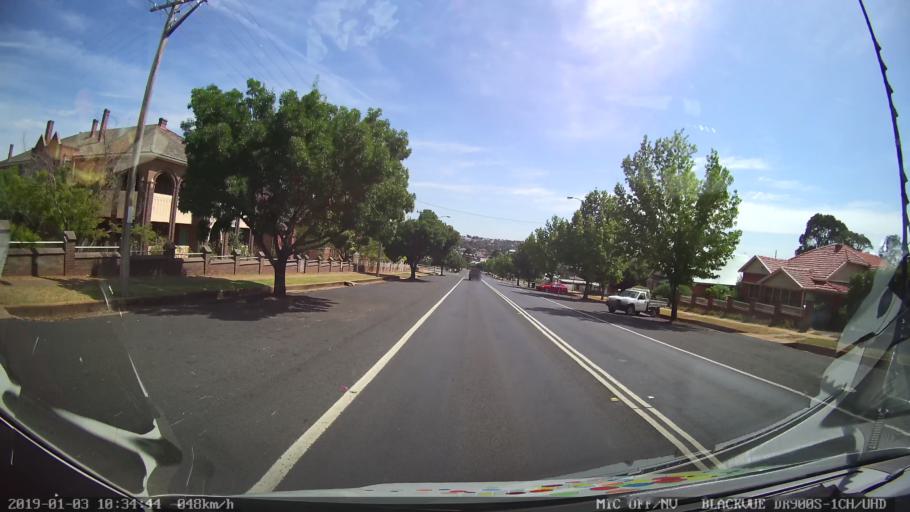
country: AU
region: New South Wales
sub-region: Young
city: Young
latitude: -34.3199
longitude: 148.2921
